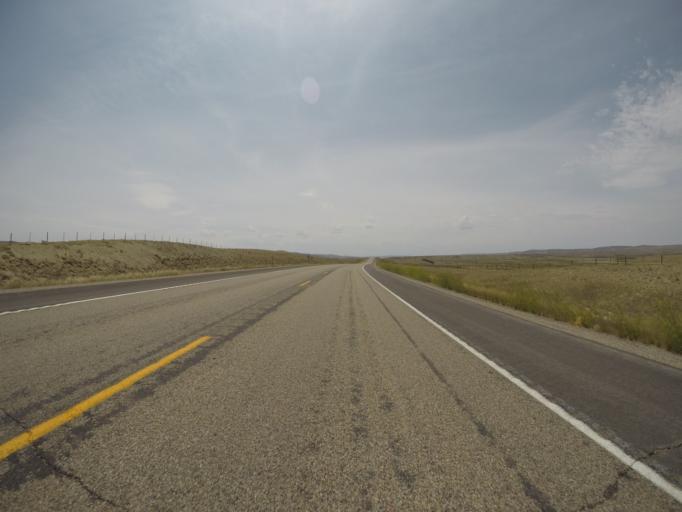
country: US
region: Wyoming
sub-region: Lincoln County
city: Kemmerer
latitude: 41.7141
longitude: -110.5656
